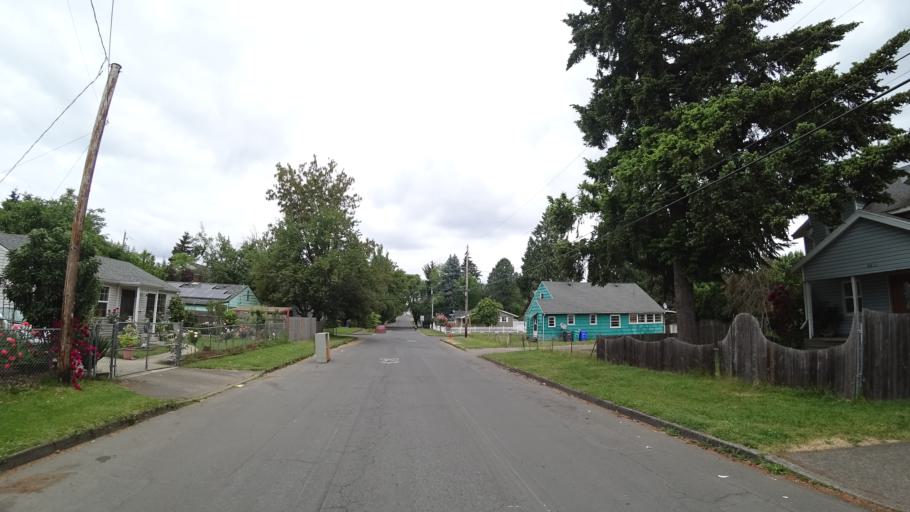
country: US
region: Oregon
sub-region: Multnomah County
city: Lents
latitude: 45.5000
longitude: -122.5750
